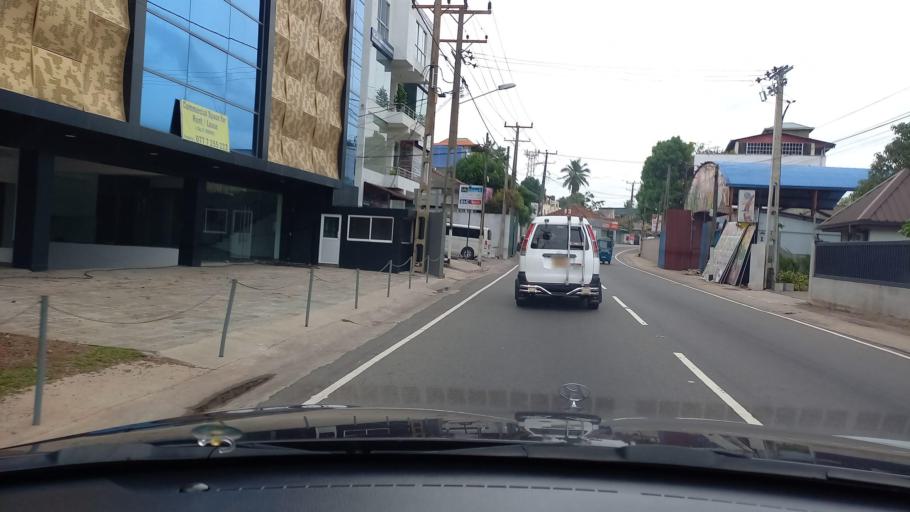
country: LK
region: Western
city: Sri Jayewardenepura Kotte
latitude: 6.8790
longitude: 79.8998
